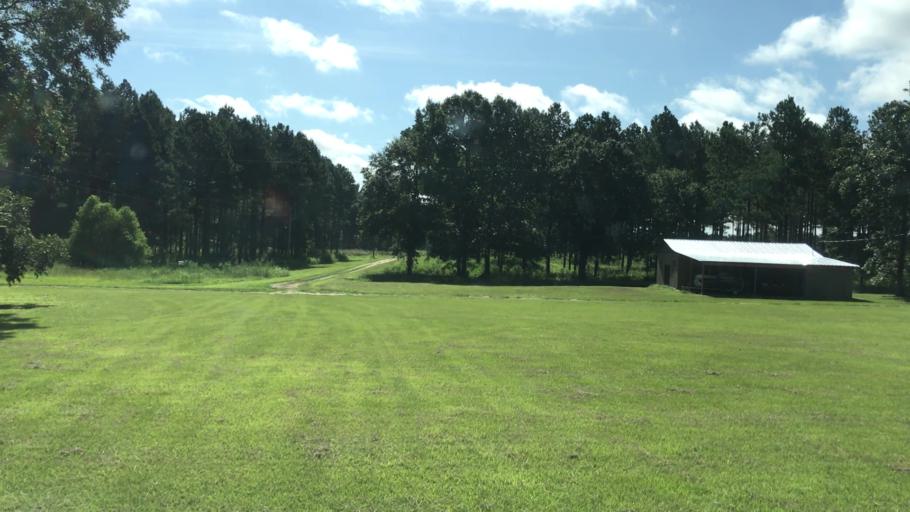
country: US
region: Georgia
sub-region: Jefferson County
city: Wadley
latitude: 32.8170
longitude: -82.3334
